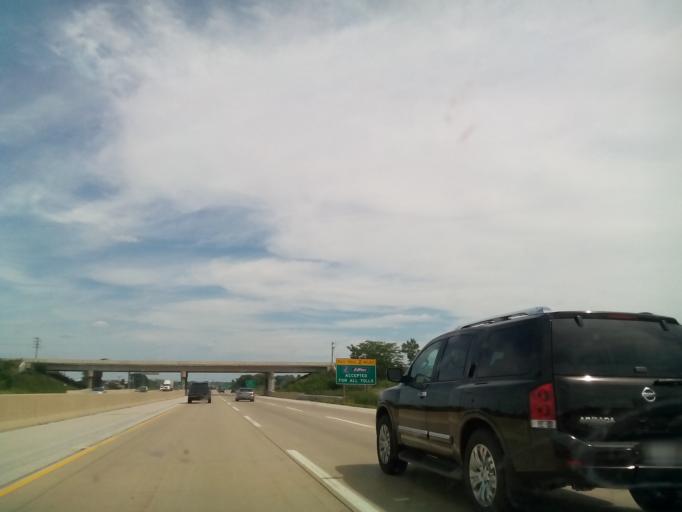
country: US
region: Illinois
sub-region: Kane County
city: North Aurora
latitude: 41.7952
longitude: -88.3518
